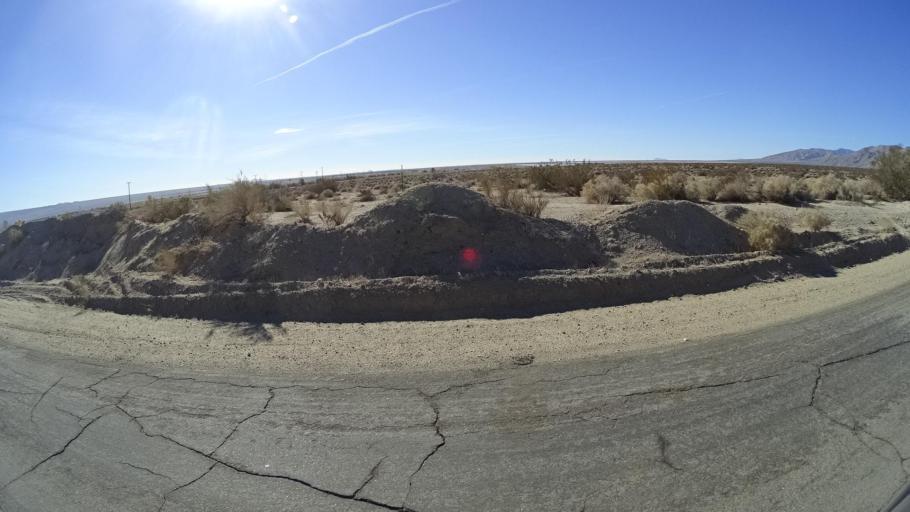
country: US
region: California
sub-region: Kern County
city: California City
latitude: 35.3014
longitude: -117.9870
